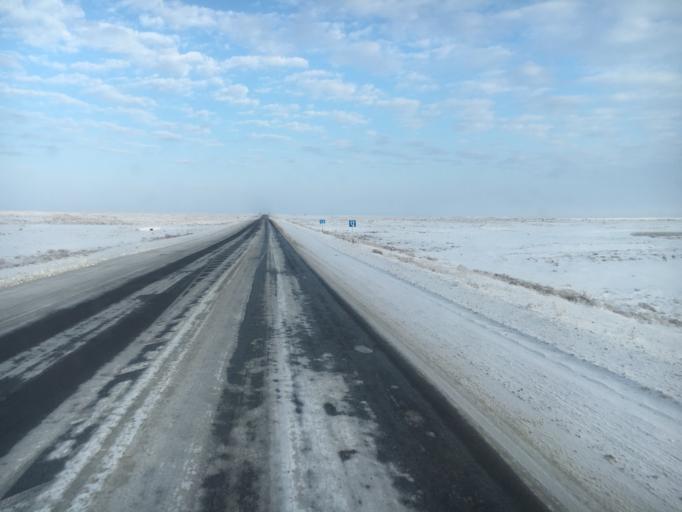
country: KZ
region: Qyzylorda
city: Sekseuil
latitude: 47.7836
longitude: 61.3480
